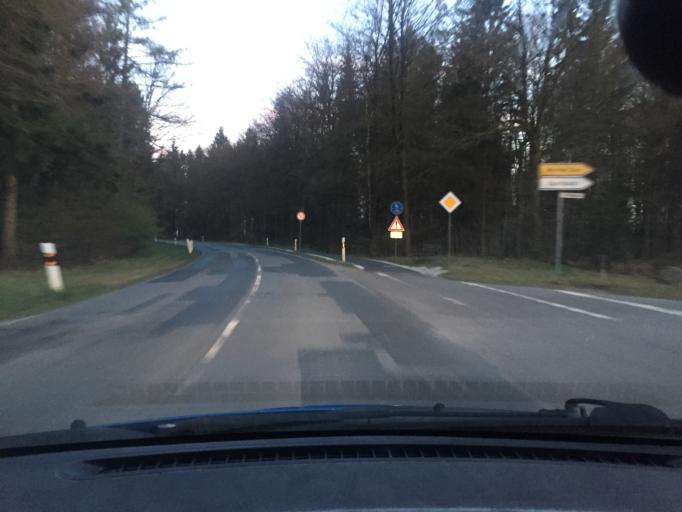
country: DE
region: Lower Saxony
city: Handeloh
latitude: 53.2683
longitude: 9.8782
